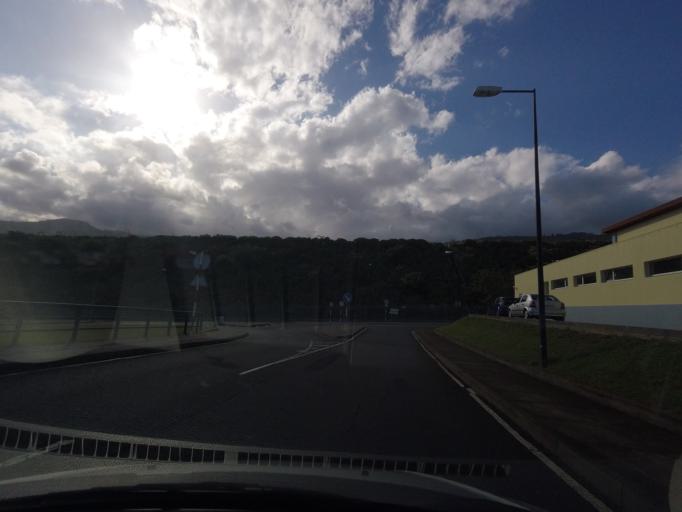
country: PT
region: Madeira
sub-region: Machico
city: Machico
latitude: 32.6901
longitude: -16.7810
